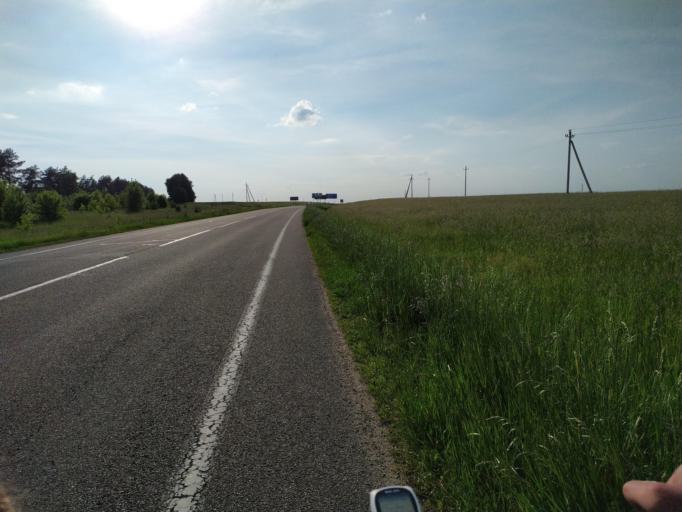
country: BY
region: Brest
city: Kamyanyets
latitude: 52.4023
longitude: 23.8693
